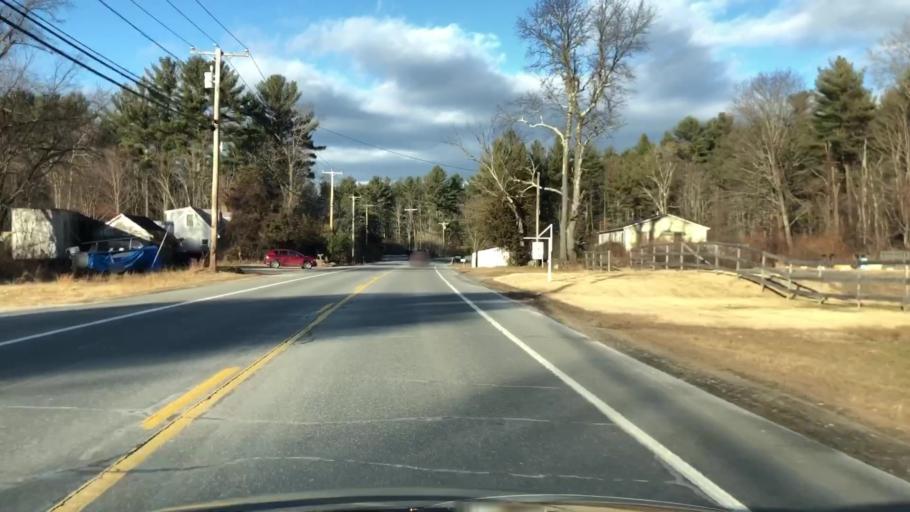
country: US
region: New Hampshire
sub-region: Hillsborough County
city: Brookline
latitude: 42.7682
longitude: -71.6738
